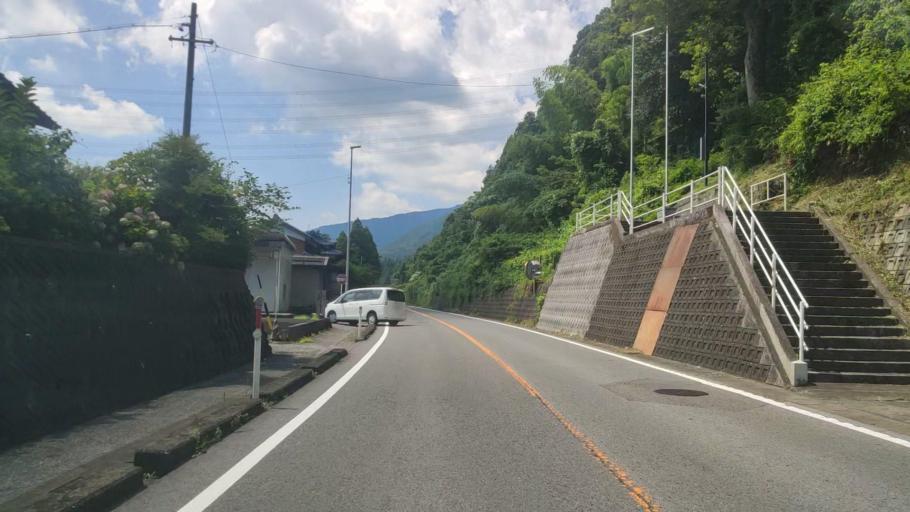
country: JP
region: Gifu
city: Tarui
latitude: 35.3776
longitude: 136.4411
